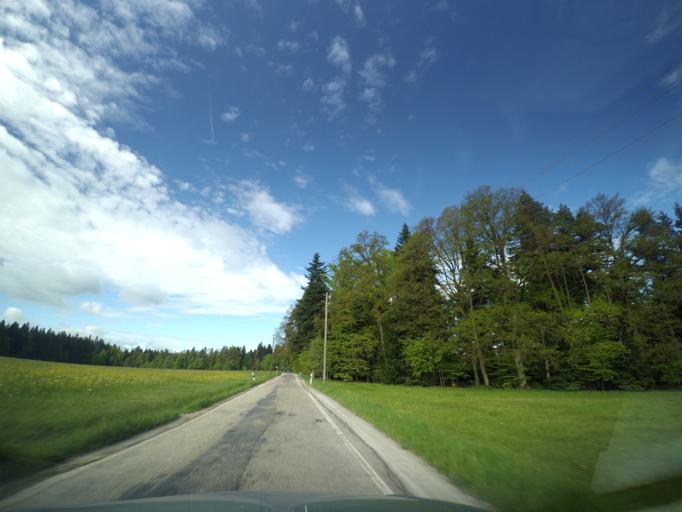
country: DE
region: Baden-Wuerttemberg
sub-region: Regierungsbezirk Stuttgart
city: Fichtenberg
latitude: 48.9763
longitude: 9.6823
